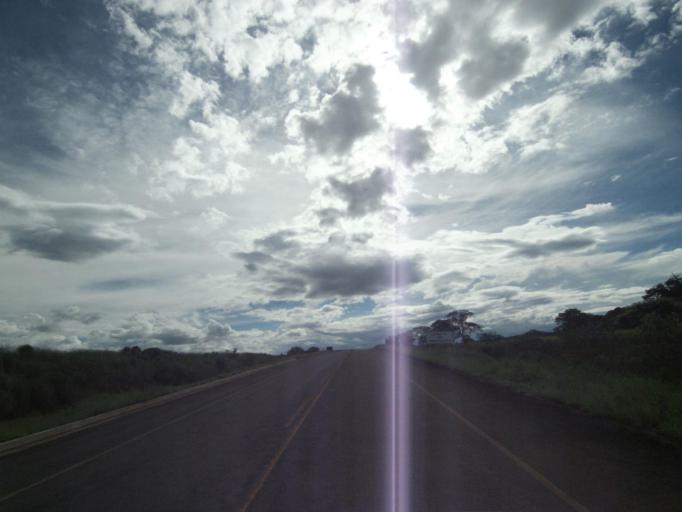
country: BR
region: Goias
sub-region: Jaragua
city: Jaragua
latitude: -15.8382
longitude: -49.2815
